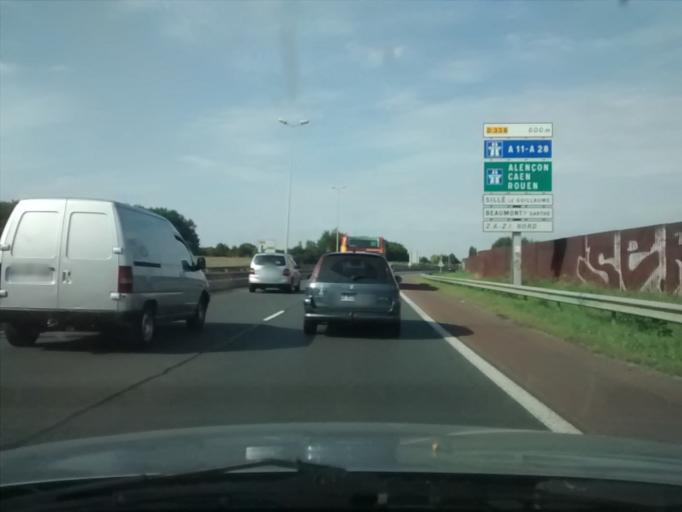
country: FR
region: Pays de la Loire
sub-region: Departement de la Sarthe
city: La Chapelle-Saint-Aubin
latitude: 48.0233
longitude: 0.1688
